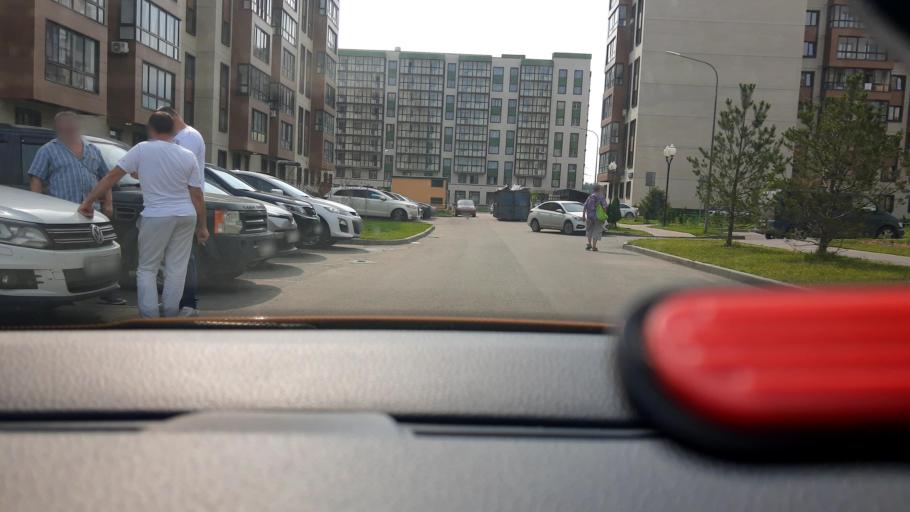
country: RU
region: Moskovskaya
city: Pirogovskiy
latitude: 55.9870
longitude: 37.7257
